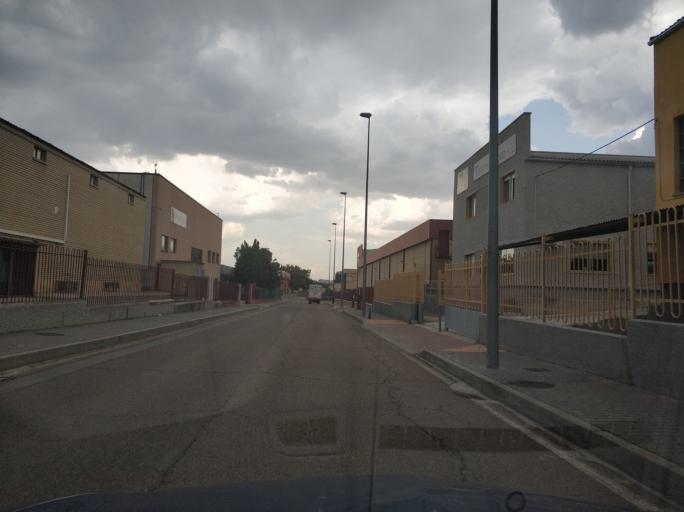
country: ES
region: Castille and Leon
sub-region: Provincia de Salamanca
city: Carbajosa de la Sagrada
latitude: 40.9430
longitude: -5.6626
